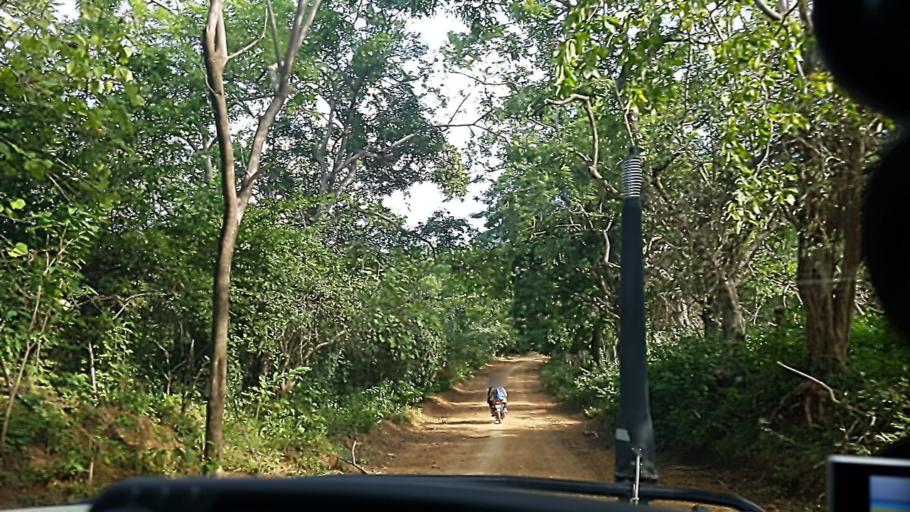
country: NI
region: Rivas
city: Tola
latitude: 11.5216
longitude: -86.1391
